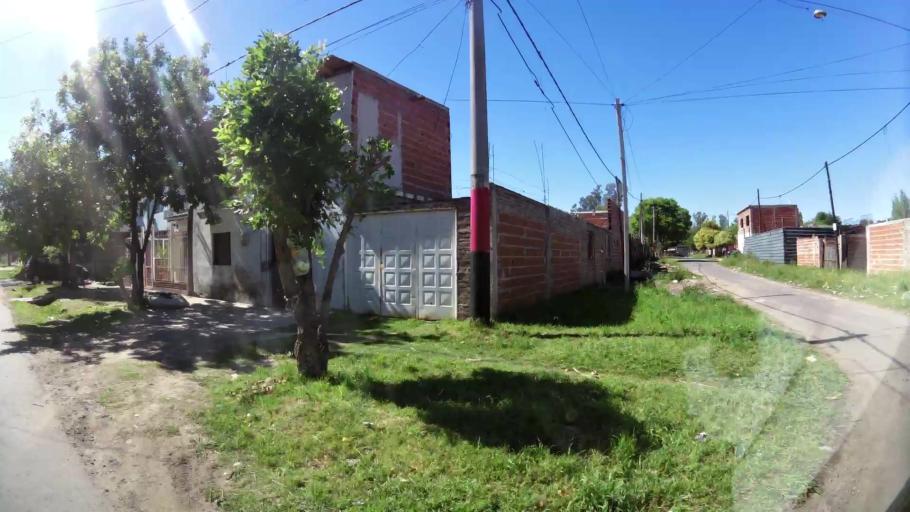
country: AR
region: Santa Fe
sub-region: Departamento de Rosario
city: Rosario
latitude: -32.9671
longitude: -60.6969
